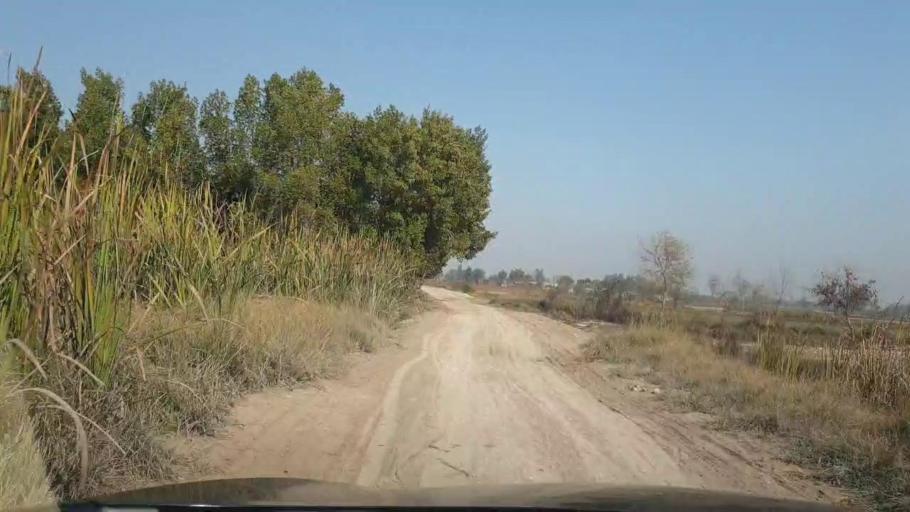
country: PK
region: Sindh
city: Ubauro
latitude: 28.1465
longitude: 69.7562
